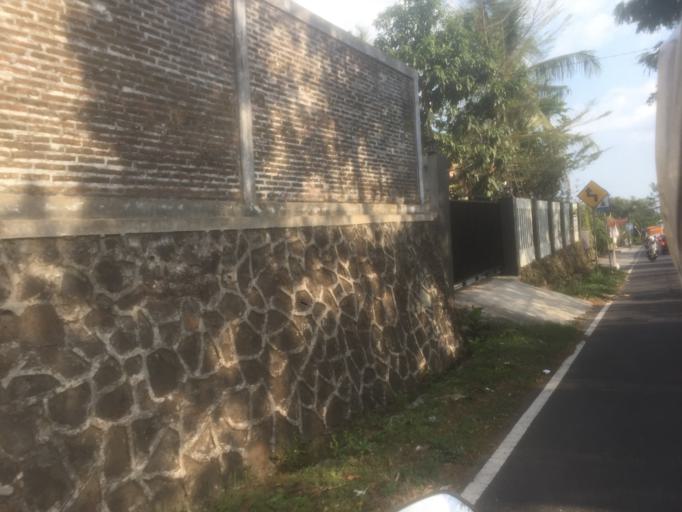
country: ID
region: Daerah Istimewa Yogyakarta
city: Sleman
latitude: -7.6530
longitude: 110.4232
